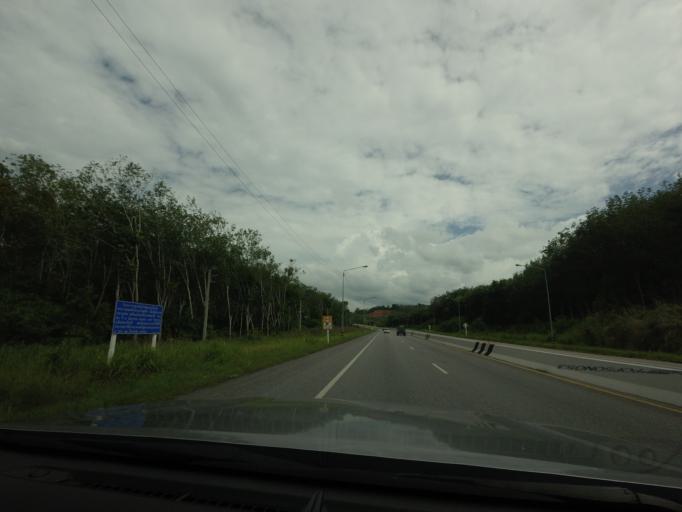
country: TH
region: Pattani
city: Mae Lan
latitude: 6.6116
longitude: 101.2394
